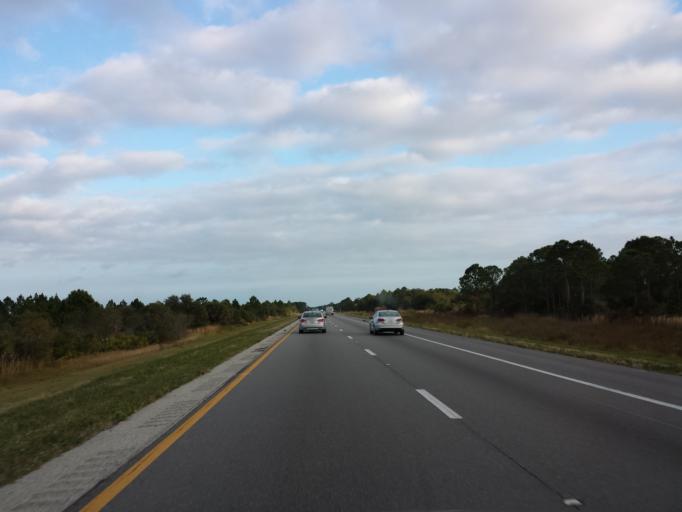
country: US
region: Florida
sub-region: Sarasota County
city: Warm Mineral Springs
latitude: 27.1086
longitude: -82.3088
